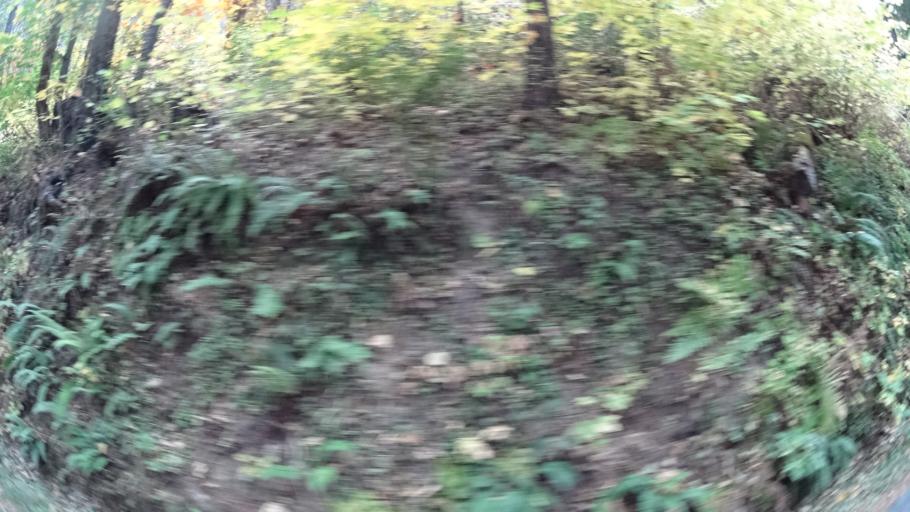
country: US
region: California
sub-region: Siskiyou County
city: Happy Camp
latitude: 41.7819
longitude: -123.3156
